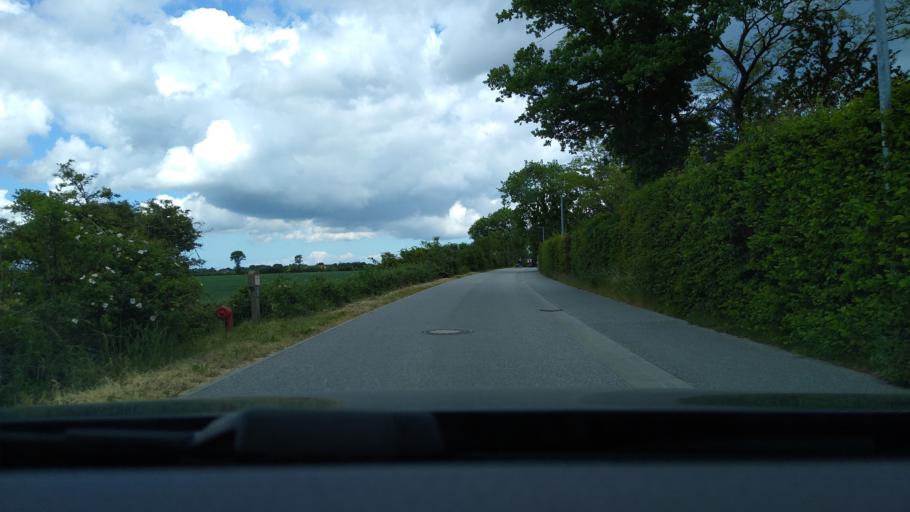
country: DE
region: Schleswig-Holstein
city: Dahme
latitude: 54.2080
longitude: 11.0894
